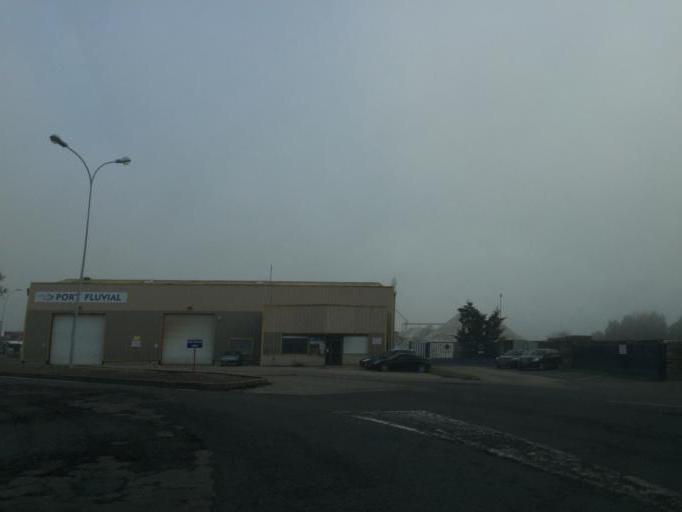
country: FR
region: Rhone-Alpes
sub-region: Departement de l'Ain
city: Jassans-Riottier
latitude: 45.9954
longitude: 4.7437
